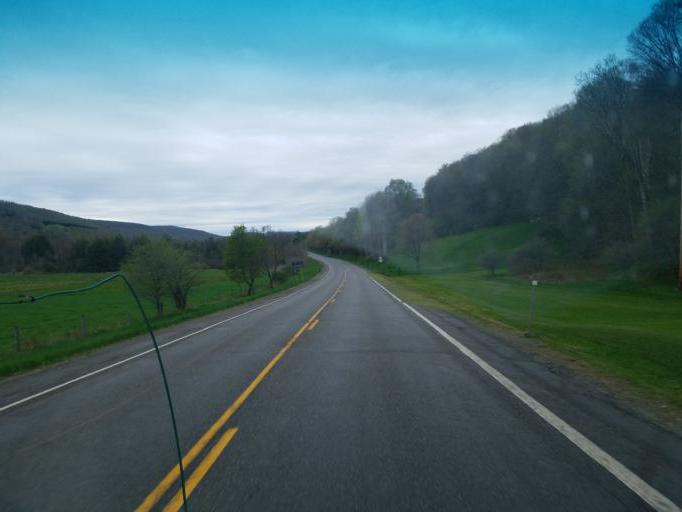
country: US
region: New York
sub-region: Allegany County
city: Andover
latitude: 42.0244
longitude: -77.8143
